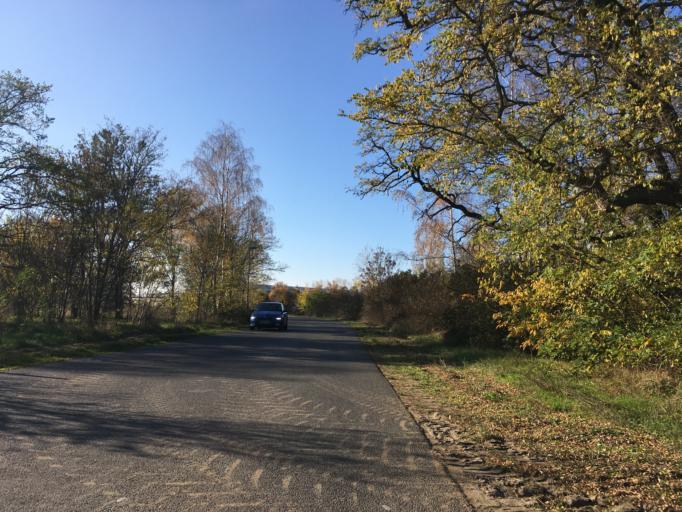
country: DE
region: Brandenburg
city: Spreenhagen
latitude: 52.3405
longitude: 13.8897
